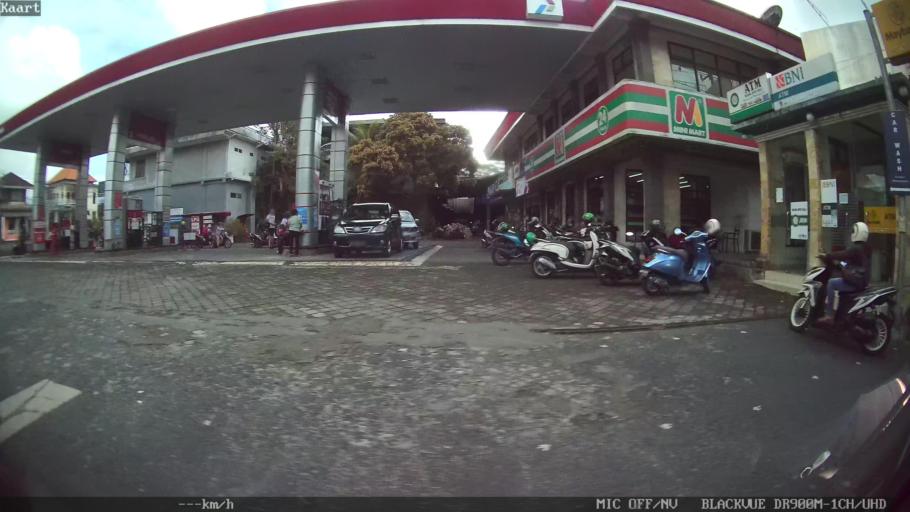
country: ID
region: Bali
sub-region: Kabupaten Gianyar
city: Ubud
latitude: -8.5248
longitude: 115.2637
